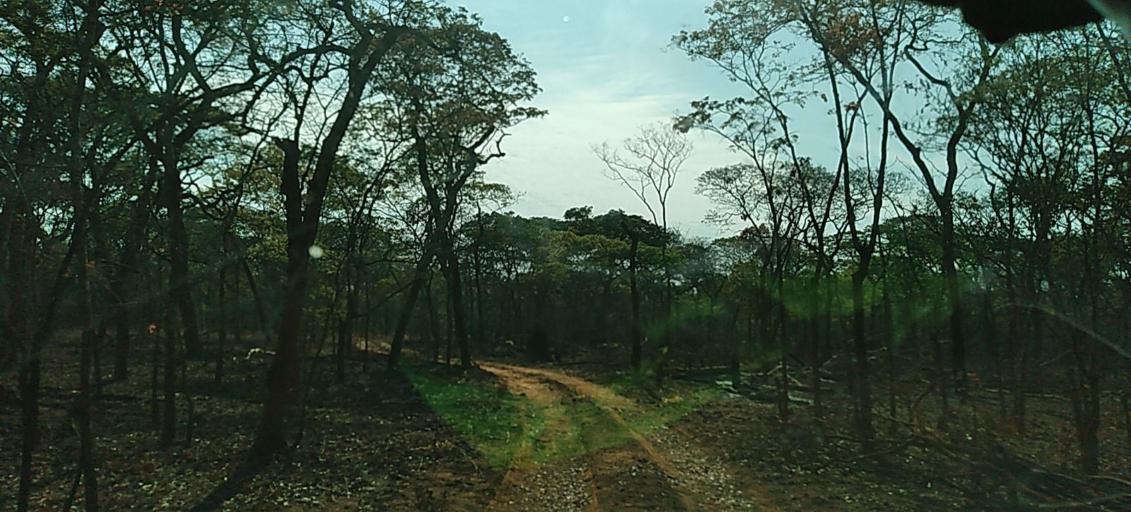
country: ZM
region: North-Western
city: Kalengwa
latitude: -13.2268
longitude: 25.0918
